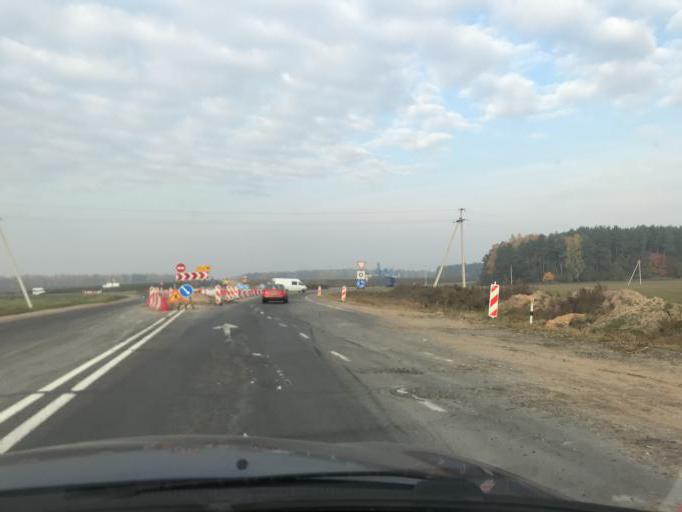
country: BY
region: Grodnenskaya
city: Lida
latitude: 53.8294
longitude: 25.3600
